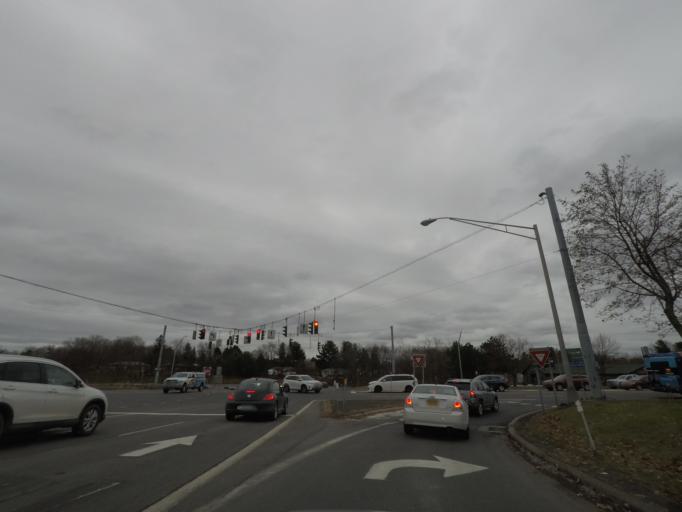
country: US
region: New York
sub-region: Albany County
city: Cohoes
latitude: 42.7582
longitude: -73.7580
